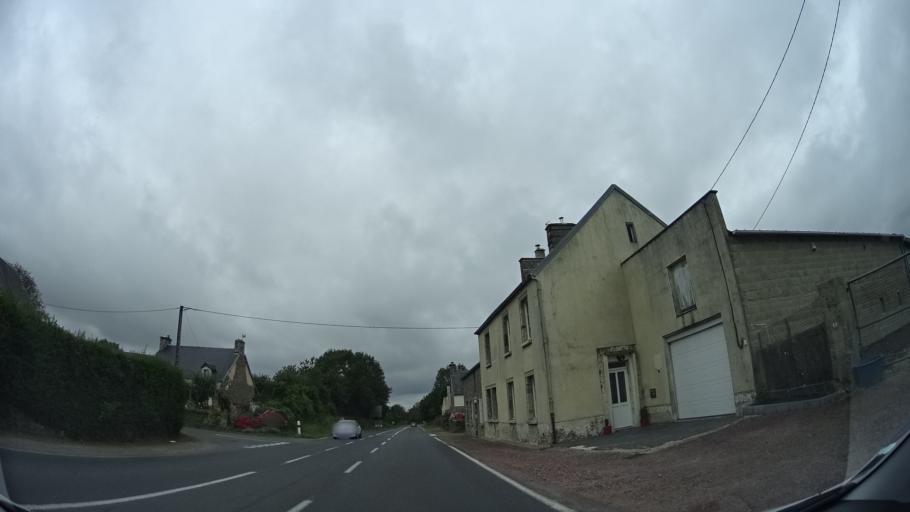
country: FR
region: Lower Normandy
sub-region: Departement de la Manche
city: La Haye-du-Puits
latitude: 49.2956
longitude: -1.5594
